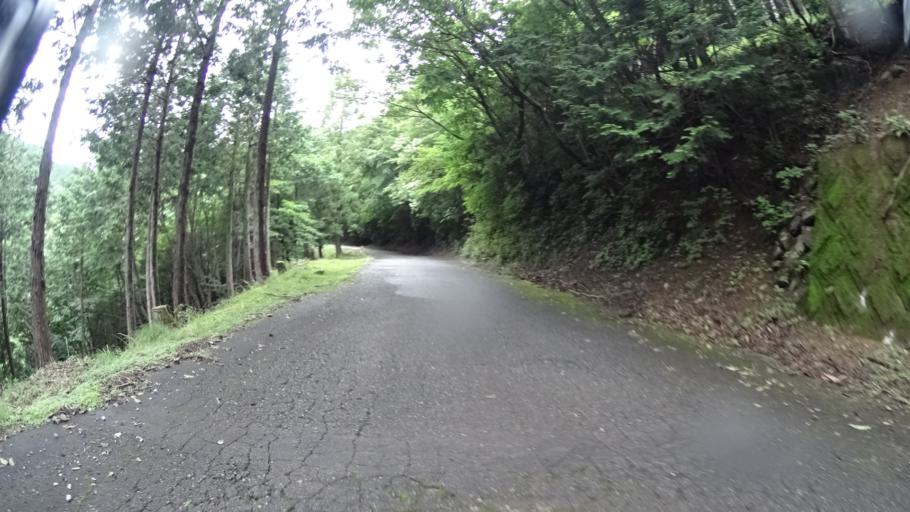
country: JP
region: Saitama
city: Chichibu
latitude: 35.8933
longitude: 139.1293
